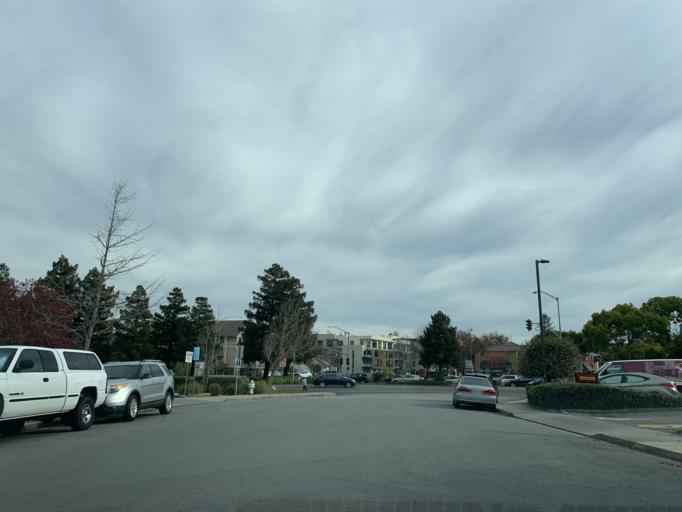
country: US
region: California
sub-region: Santa Clara County
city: Mountain View
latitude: 37.3919
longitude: -122.0965
